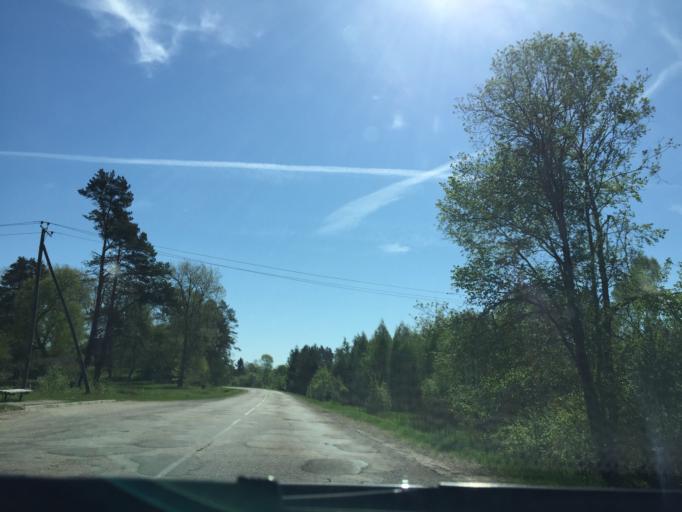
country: LV
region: Ropazu
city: Ropazi
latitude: 57.0073
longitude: 24.5717
